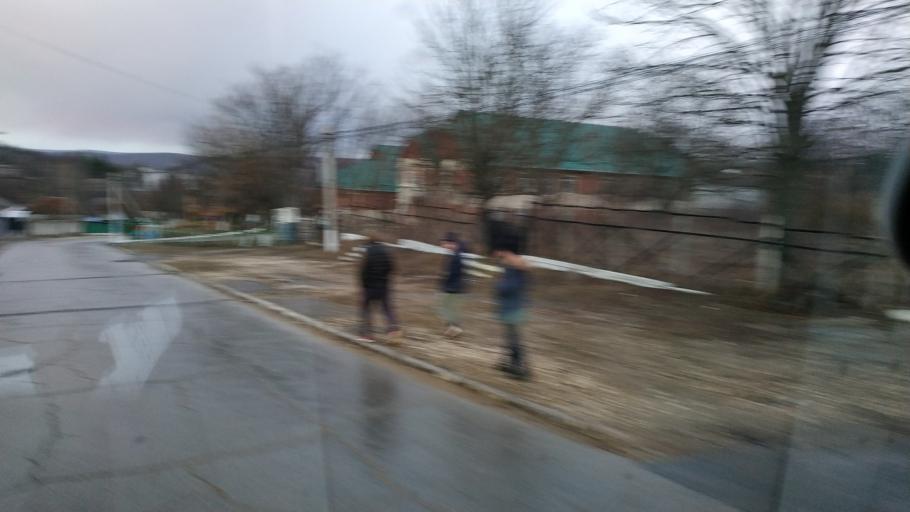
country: MD
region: Calarasi
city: Calarasi
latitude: 47.3739
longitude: 28.3205
